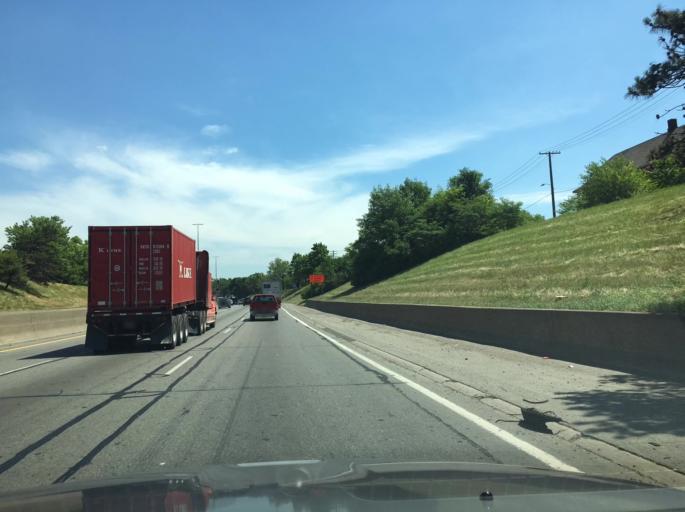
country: US
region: Michigan
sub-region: Wayne County
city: Dearborn
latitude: 42.3385
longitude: -83.1218
